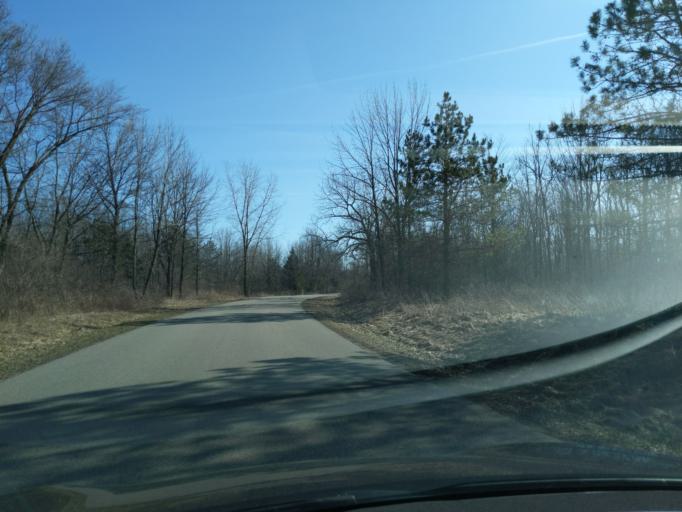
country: US
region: Michigan
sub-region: Ionia County
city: Saranac
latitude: 42.9356
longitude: -85.1343
